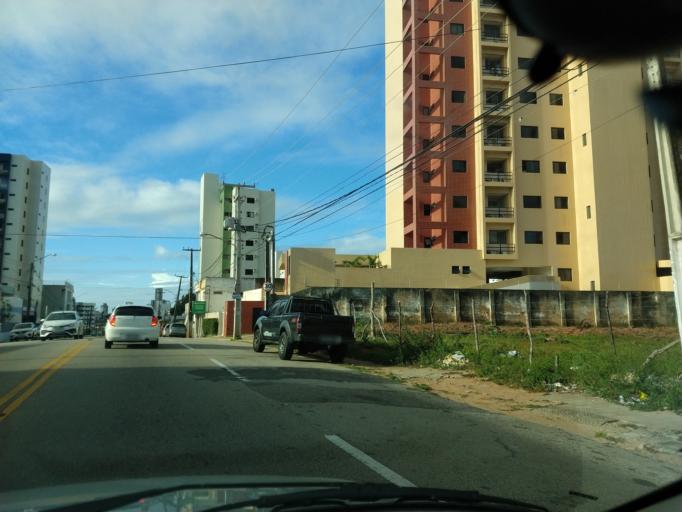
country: BR
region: Rio Grande do Norte
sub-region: Natal
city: Natal
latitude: -5.7970
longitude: -35.2099
